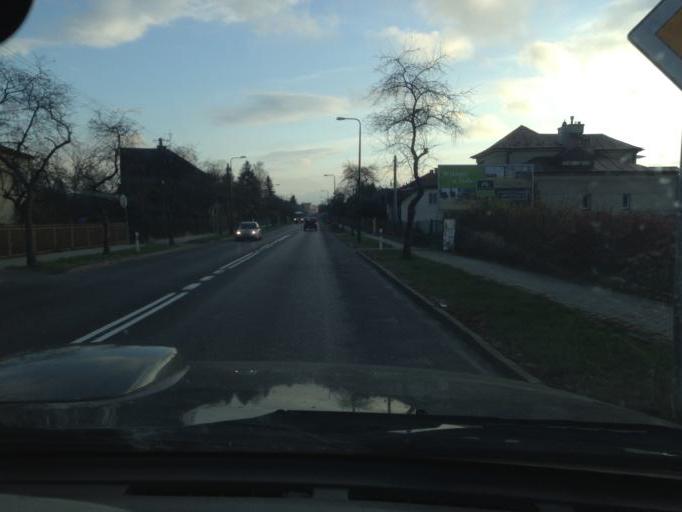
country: PL
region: Subcarpathian Voivodeship
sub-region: Powiat jasielski
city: Jaslo
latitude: 49.7585
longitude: 21.4715
